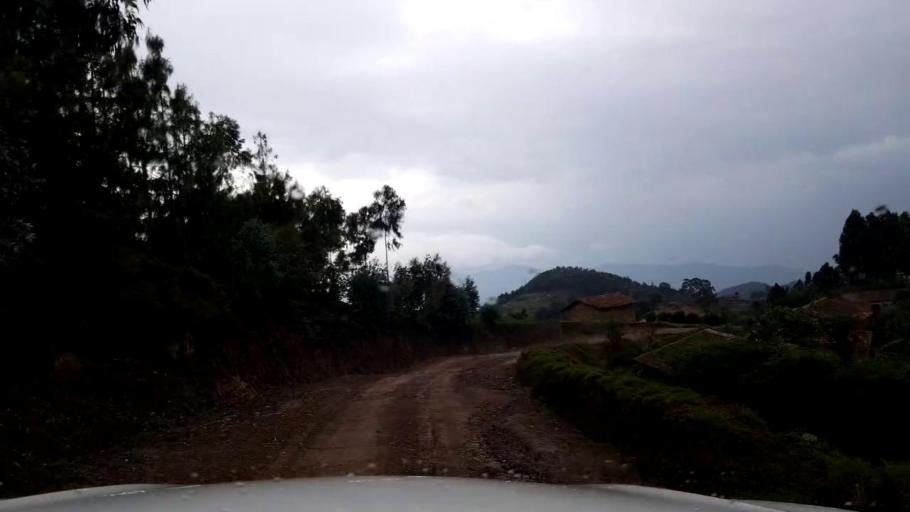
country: RW
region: Western Province
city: Kibuye
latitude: -2.0145
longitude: 29.4682
